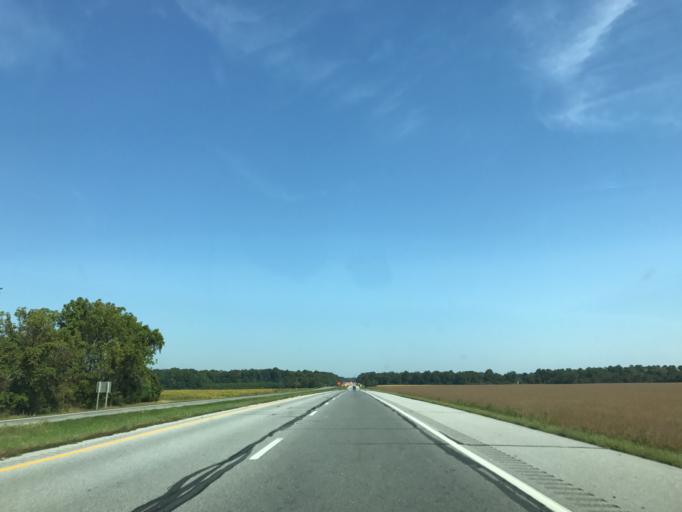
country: US
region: Delaware
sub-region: New Castle County
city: Middletown
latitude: 39.3961
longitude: -75.7870
